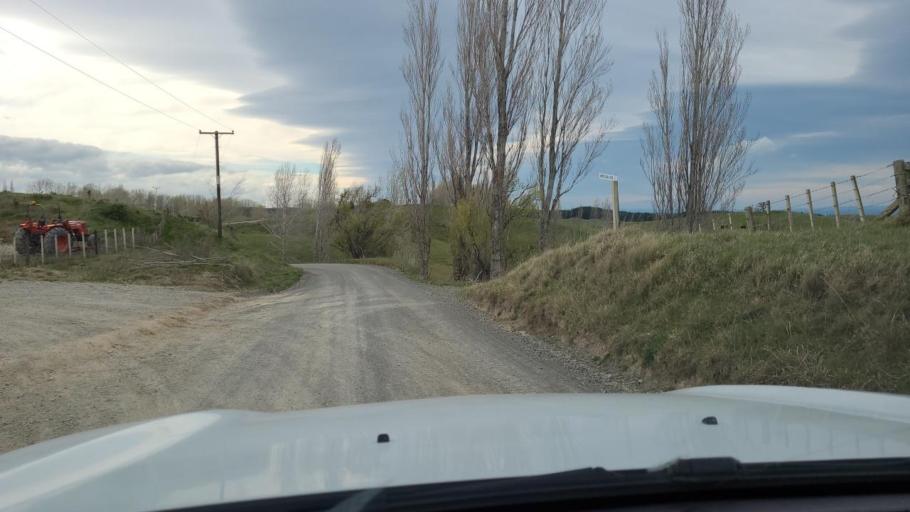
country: NZ
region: Hawke's Bay
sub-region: Napier City
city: Napier
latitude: -39.3478
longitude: 176.8274
